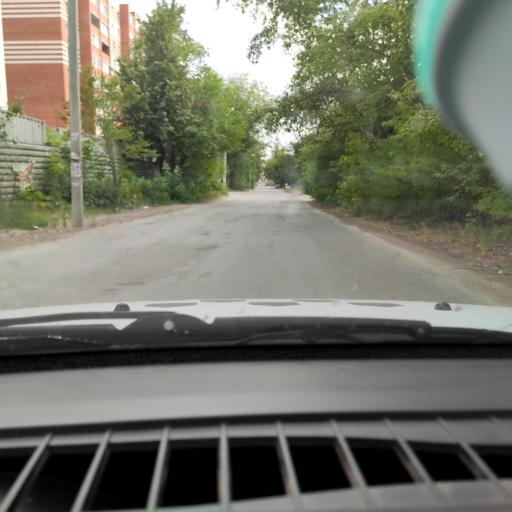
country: RU
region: Chelyabinsk
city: Miass
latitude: 55.0640
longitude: 60.1109
